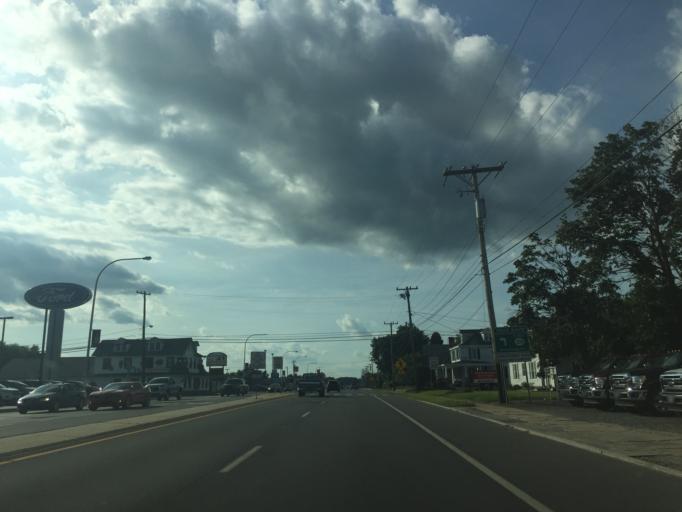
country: US
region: Delaware
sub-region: Kent County
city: Smyrna
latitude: 39.3031
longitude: -75.6041
